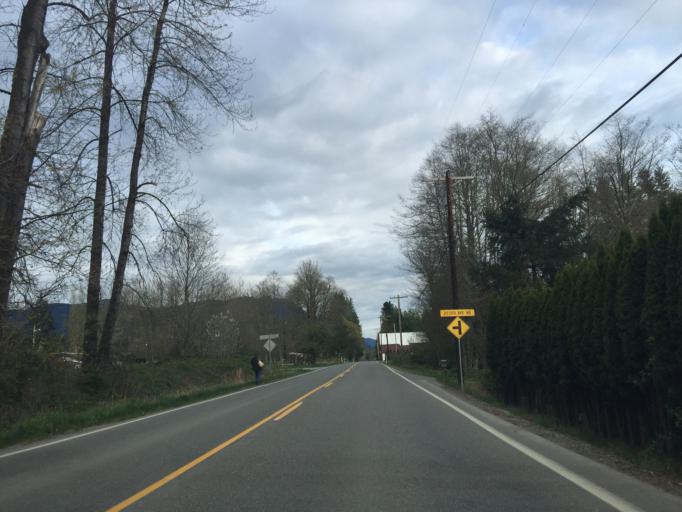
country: US
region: Washington
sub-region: Snohomish County
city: Arlington Heights
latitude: 48.2708
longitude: -121.9306
